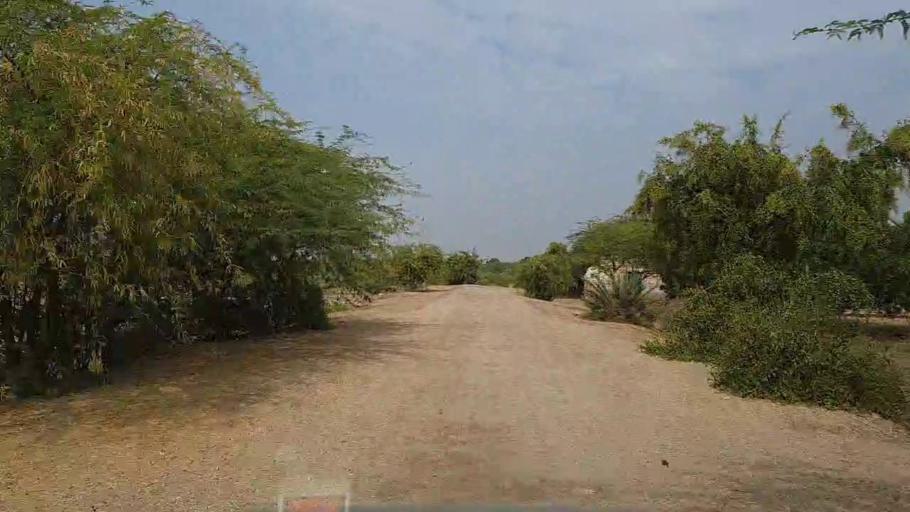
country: PK
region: Sindh
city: Mirwah Gorchani
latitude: 25.3416
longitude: 69.0411
